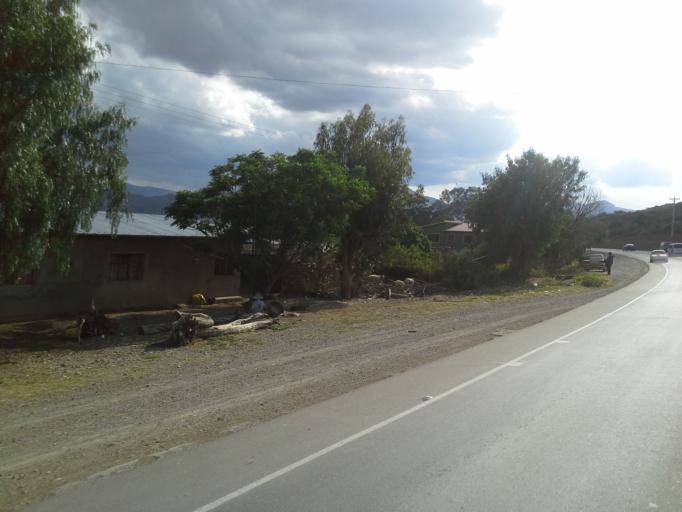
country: BO
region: Cochabamba
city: Tarata
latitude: -17.5412
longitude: -66.0379
